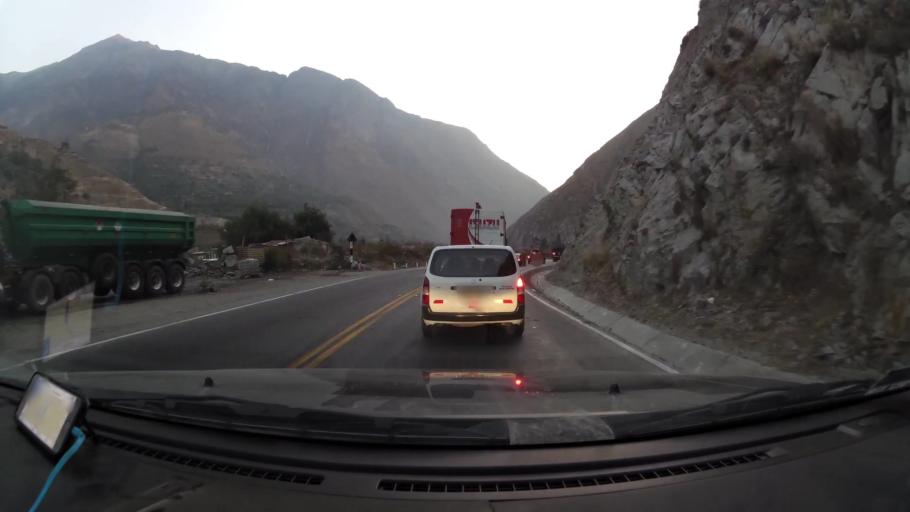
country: PE
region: Lima
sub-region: Provincia de Huarochiri
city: Surco
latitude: -11.8819
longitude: -76.4388
